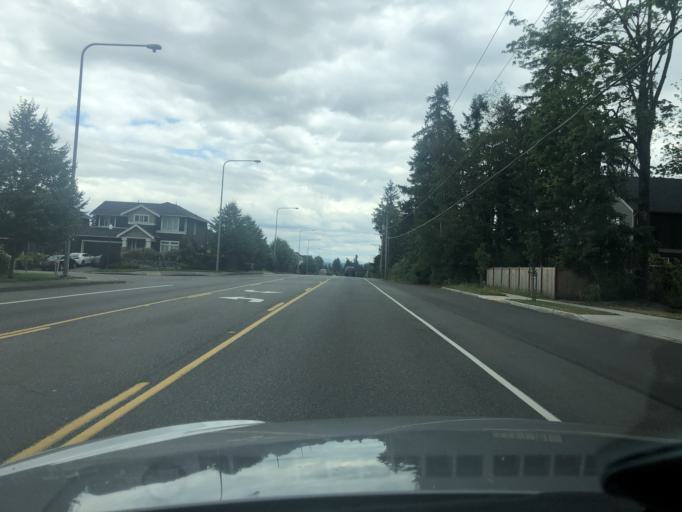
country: US
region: Washington
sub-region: King County
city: Lea Hill
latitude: 47.3278
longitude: -122.1658
